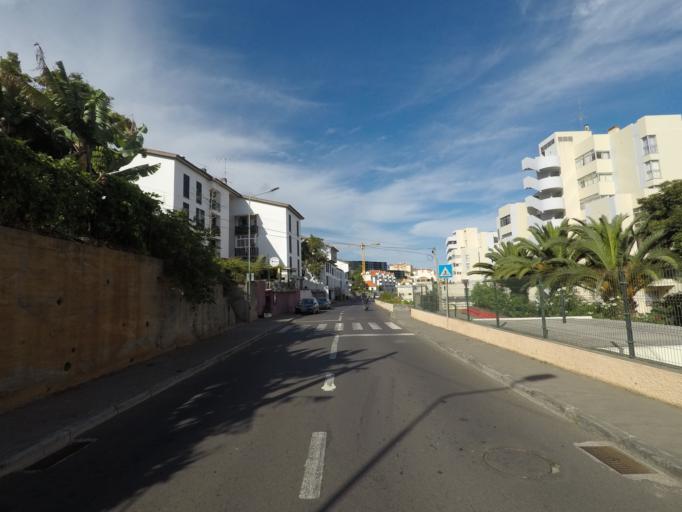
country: PT
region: Madeira
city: Camara de Lobos
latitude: 32.6387
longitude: -16.9370
